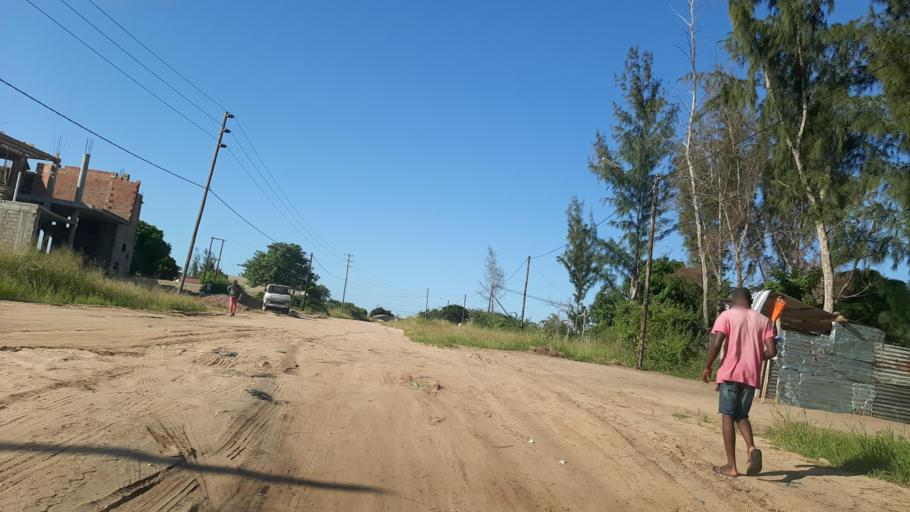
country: MZ
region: Maputo City
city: Maputo
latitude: -25.7601
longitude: 32.5493
